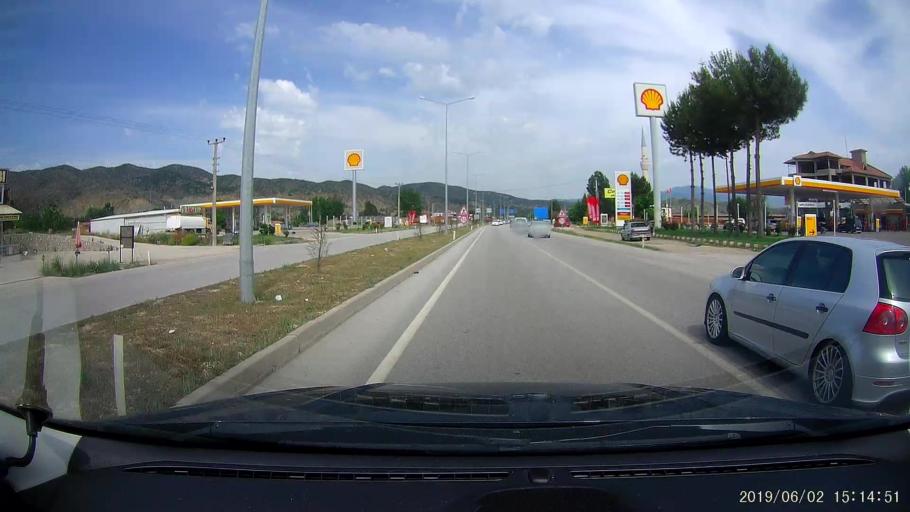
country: TR
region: Corum
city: Osmancik
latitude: 40.9708
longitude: 34.8412
